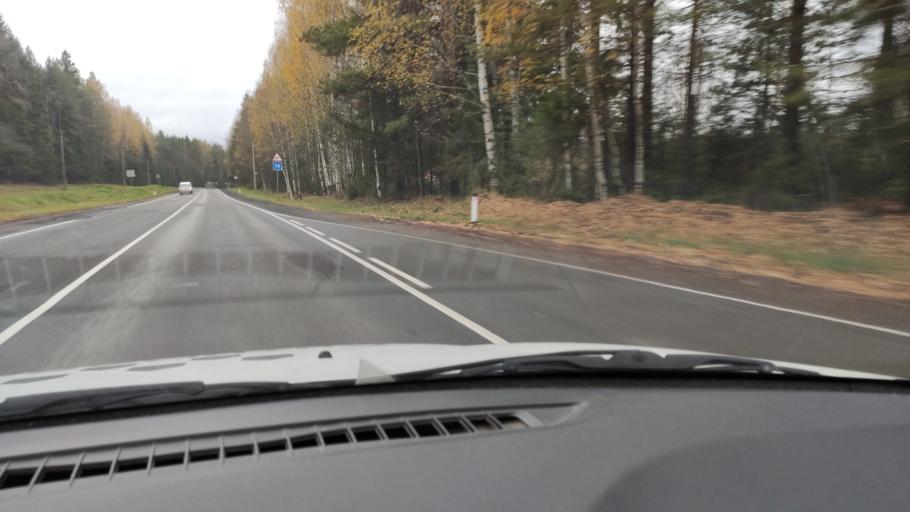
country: RU
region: Kirov
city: Belaya Kholunitsa
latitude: 58.9040
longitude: 50.9533
